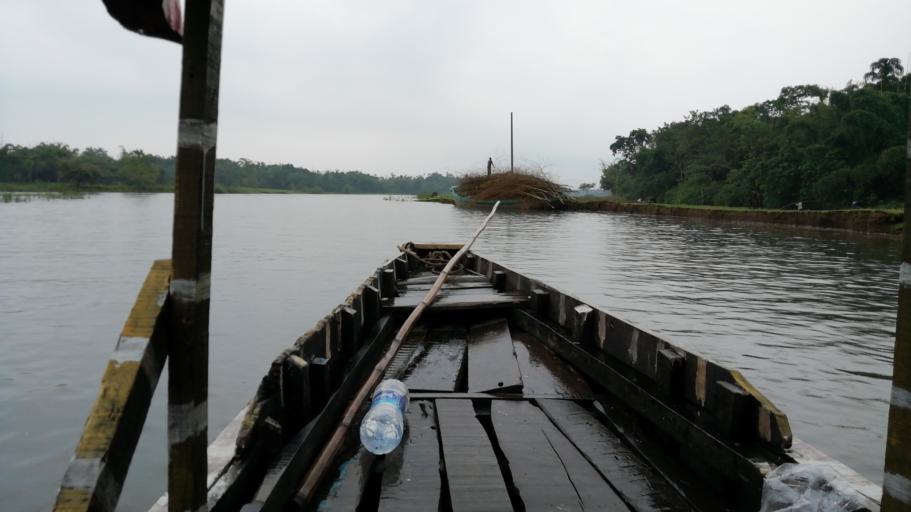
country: IN
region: Meghalaya
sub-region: East Khasi Hills
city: Cherrapunji
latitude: 25.1699
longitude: 91.9226
